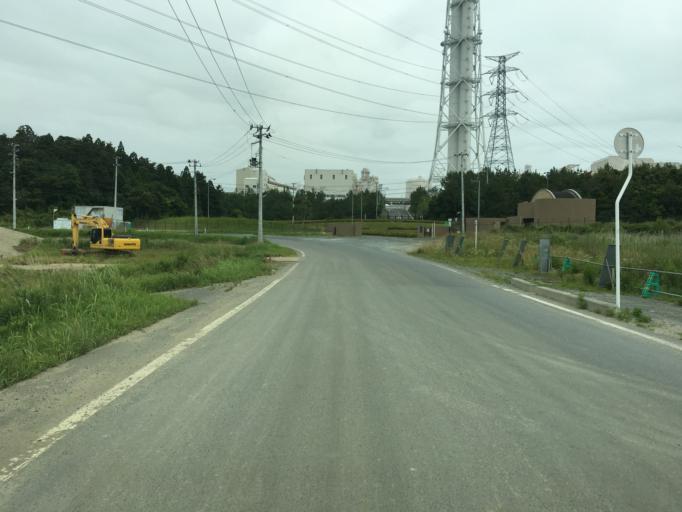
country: JP
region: Fukushima
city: Namie
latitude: 37.6618
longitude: 141.0154
